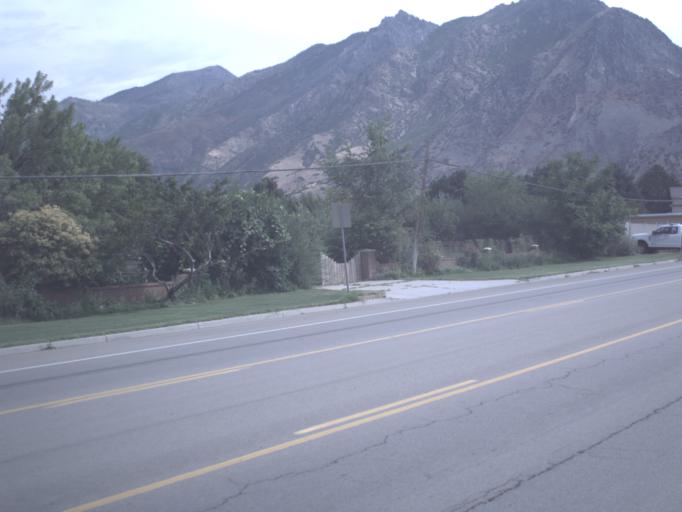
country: US
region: Utah
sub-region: Utah County
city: Highland
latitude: 40.4320
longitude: -111.7719
